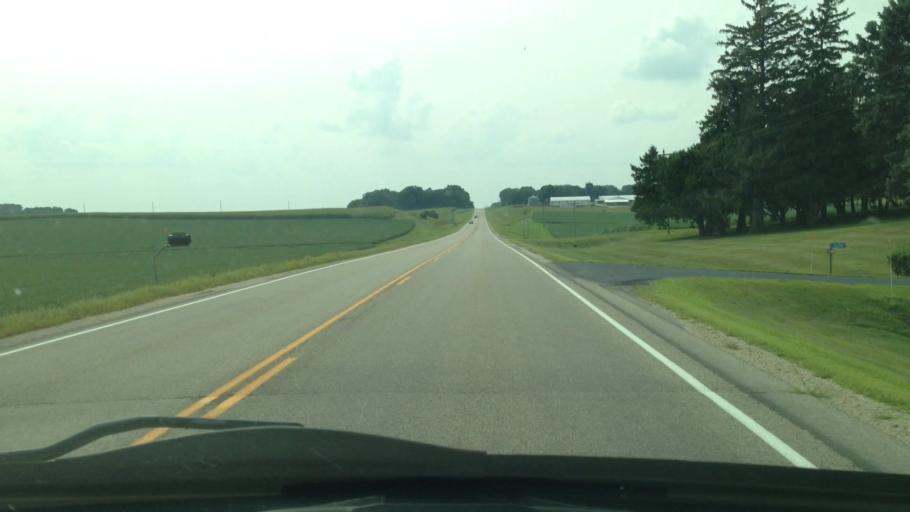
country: US
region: Minnesota
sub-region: Wabasha County
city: Plainview
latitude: 44.1652
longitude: -92.2051
